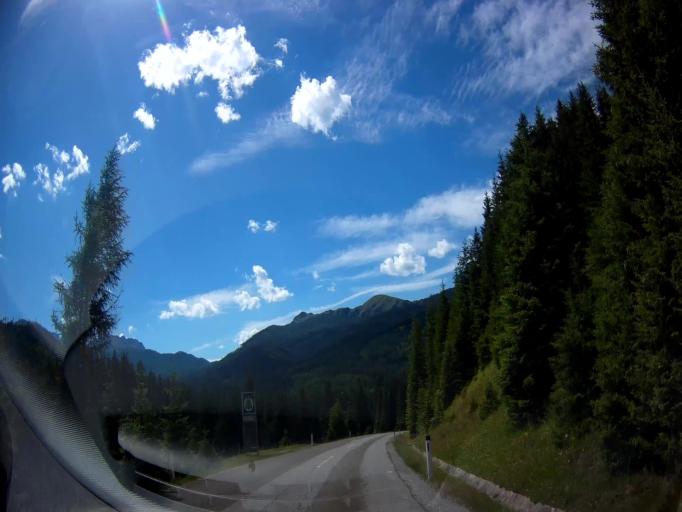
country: AT
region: Styria
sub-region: Politischer Bezirk Murau
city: Stadl an der Mur
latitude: 46.9718
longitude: 14.0138
